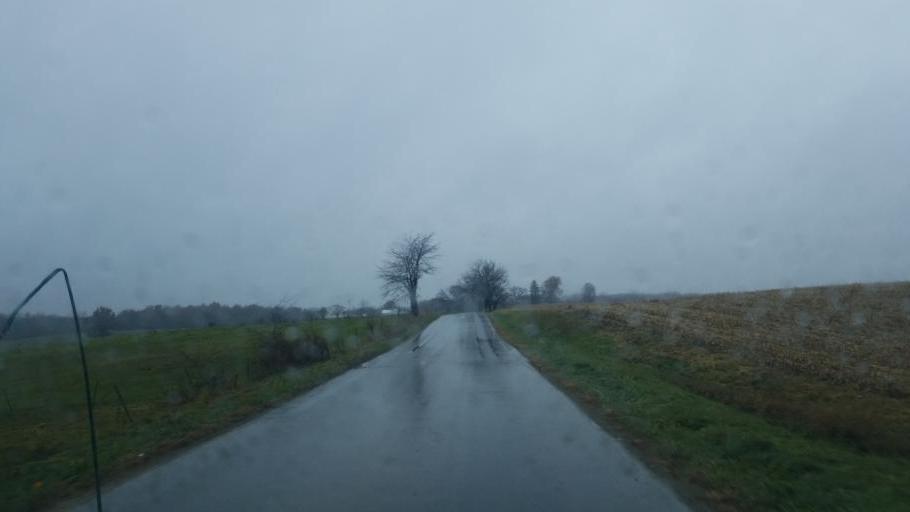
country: US
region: Indiana
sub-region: Adams County
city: Geneva
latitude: 40.6147
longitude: -84.9261
